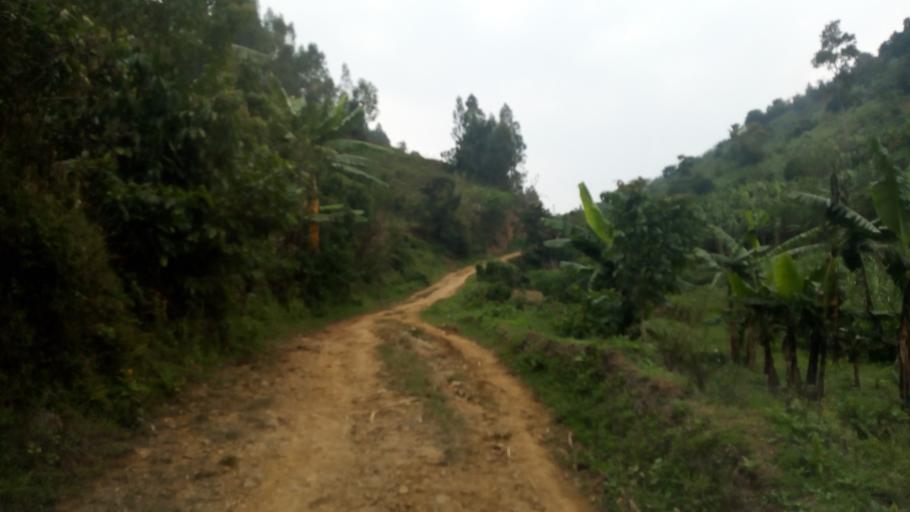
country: UG
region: Western Region
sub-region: Kisoro District
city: Kisoro
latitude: -1.2453
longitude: 29.6198
